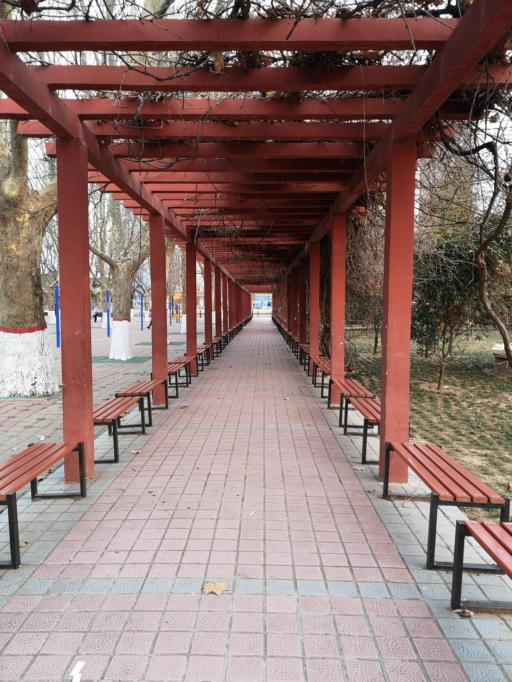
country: CN
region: Henan Sheng
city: Zhongyuanlu
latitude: 35.7748
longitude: 115.0770
